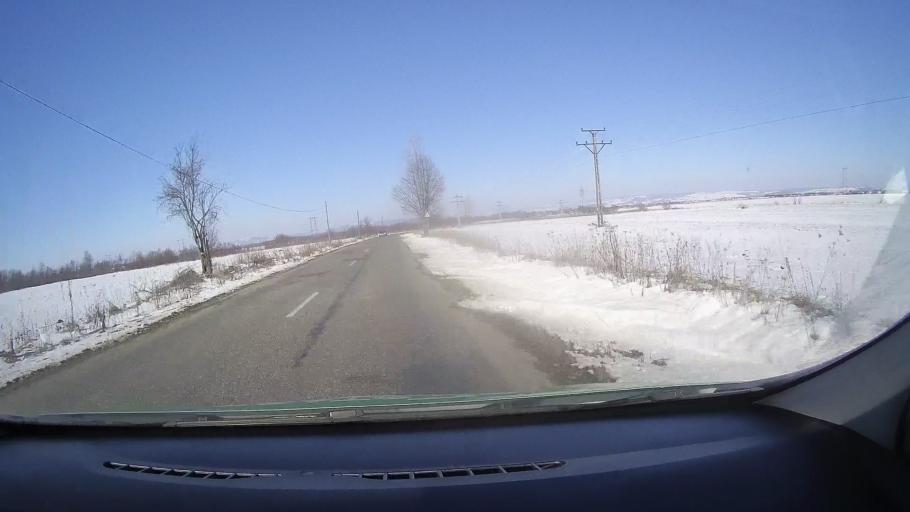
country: RO
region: Brasov
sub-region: Comuna Harseni
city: Harseni
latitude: 45.7705
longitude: 25.0020
